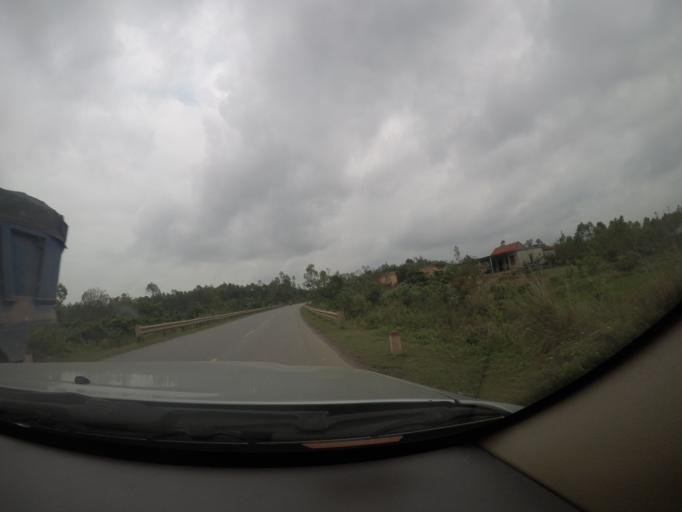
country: VN
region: Quang Binh
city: Quan Hau
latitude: 17.3395
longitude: 106.6263
